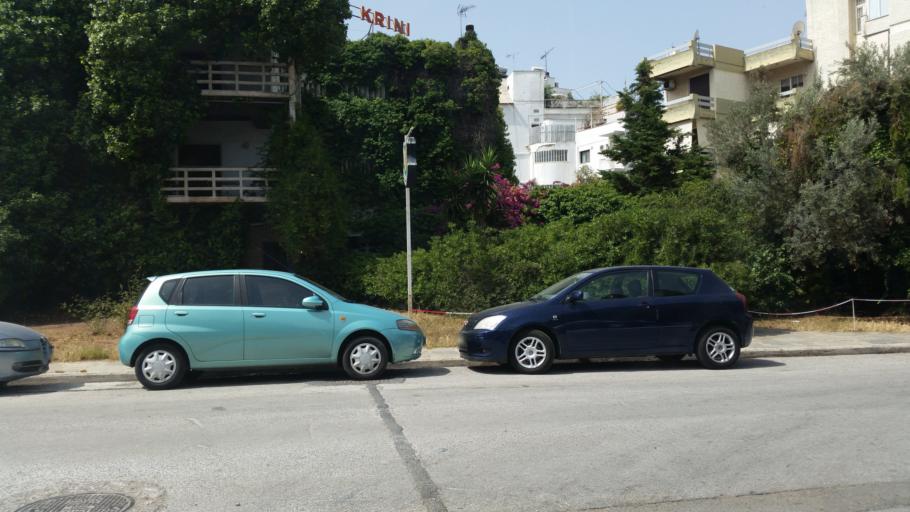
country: GR
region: Attica
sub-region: Nomarchia Athinas
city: Glyfada
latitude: 37.8559
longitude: 23.7528
